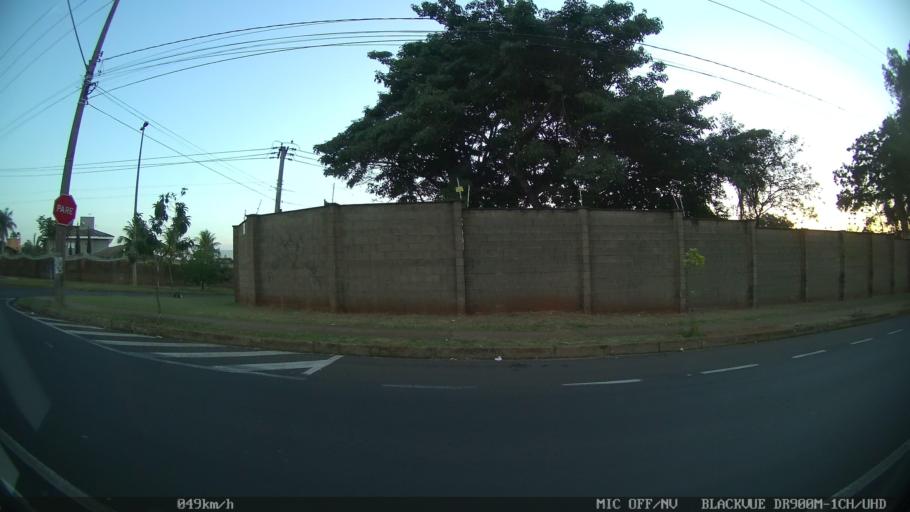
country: BR
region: Sao Paulo
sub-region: Sao Jose Do Rio Preto
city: Sao Jose do Rio Preto
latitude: -20.8087
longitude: -49.3422
